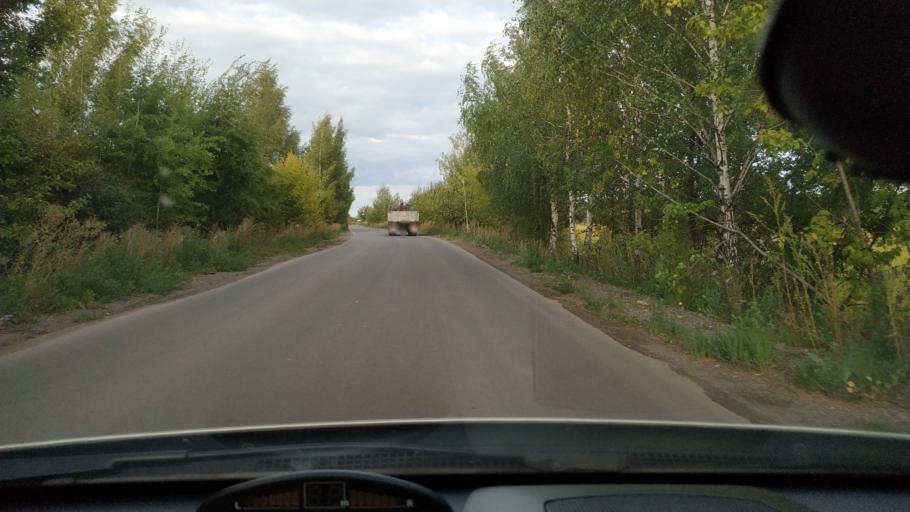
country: RU
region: Rjazan
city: Polyany
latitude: 54.5774
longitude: 39.8569
